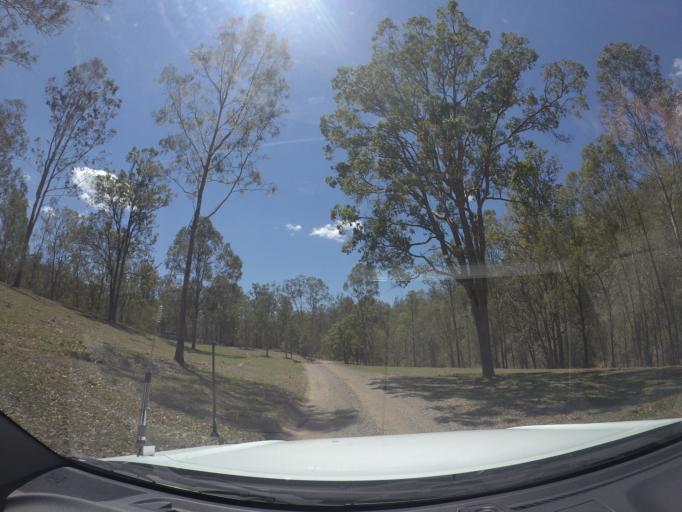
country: AU
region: Queensland
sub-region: Ipswich
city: Deebing Heights
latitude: -27.7601
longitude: 152.8102
